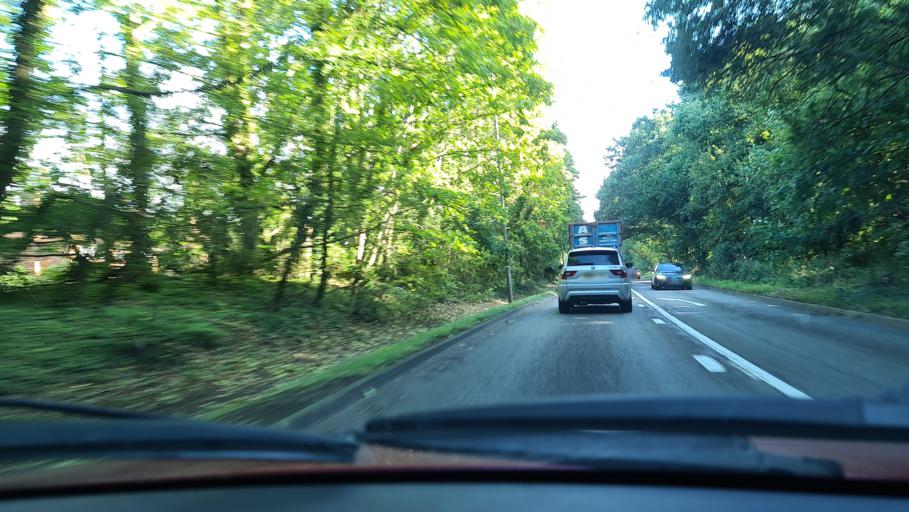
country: GB
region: England
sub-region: Buckinghamshire
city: Beaconsfield
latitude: 51.6133
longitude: -0.6330
